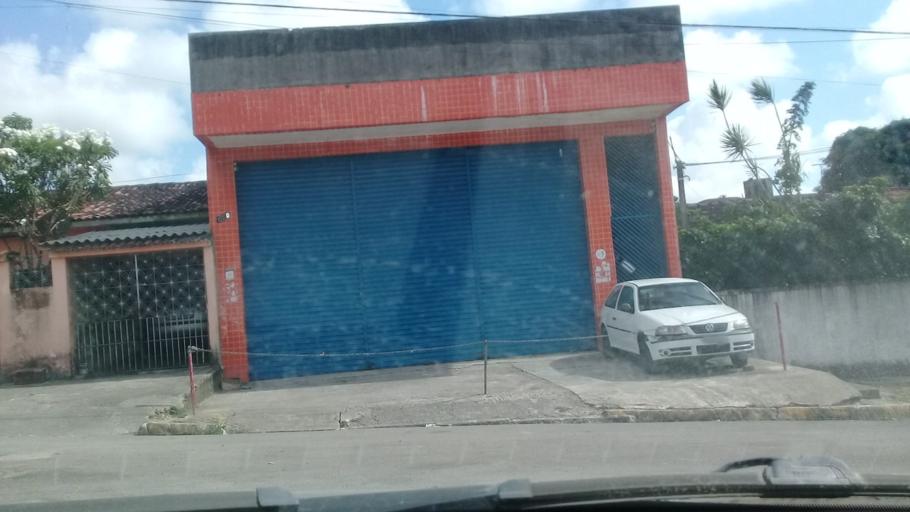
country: BR
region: Pernambuco
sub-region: Jaboatao Dos Guararapes
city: Jaboatao dos Guararapes
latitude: -8.1155
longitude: -34.9472
